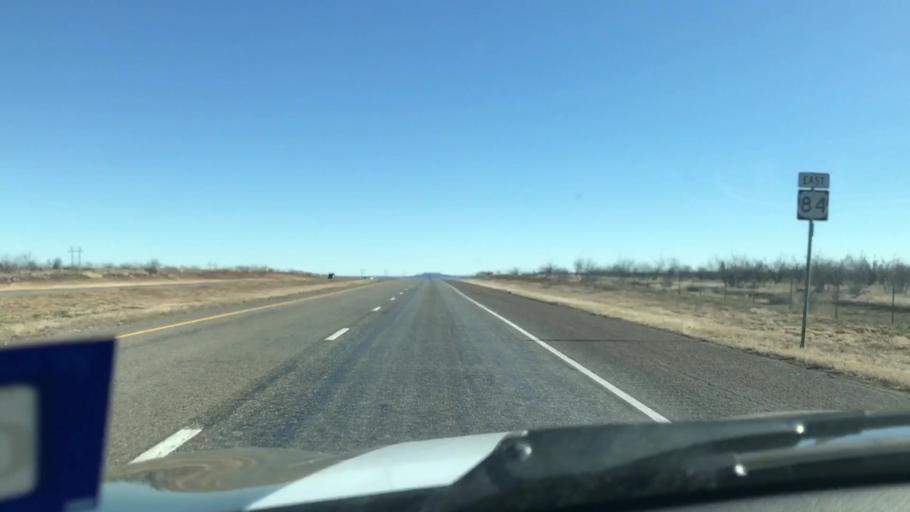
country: US
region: Texas
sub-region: Garza County
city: Post
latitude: 33.0992
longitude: -101.2568
